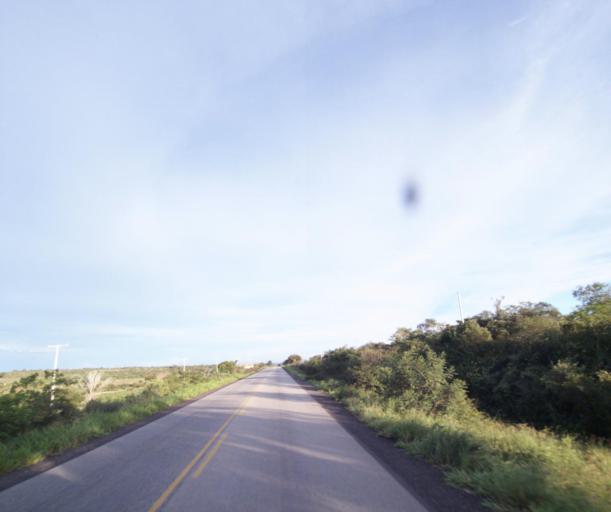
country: BR
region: Bahia
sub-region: Malhada De Pedras
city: Santana
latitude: -14.2182
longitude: -41.9994
